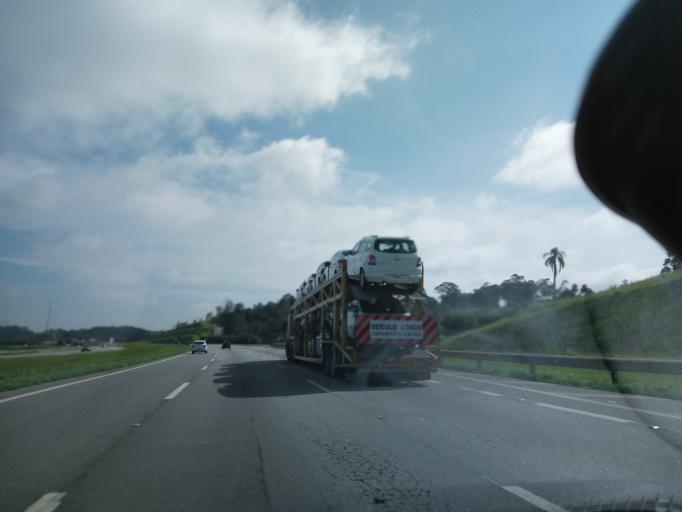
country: BR
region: Sao Paulo
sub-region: Itapecerica Da Serra
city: Itapecerica da Serra
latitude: -23.7300
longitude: -46.8089
